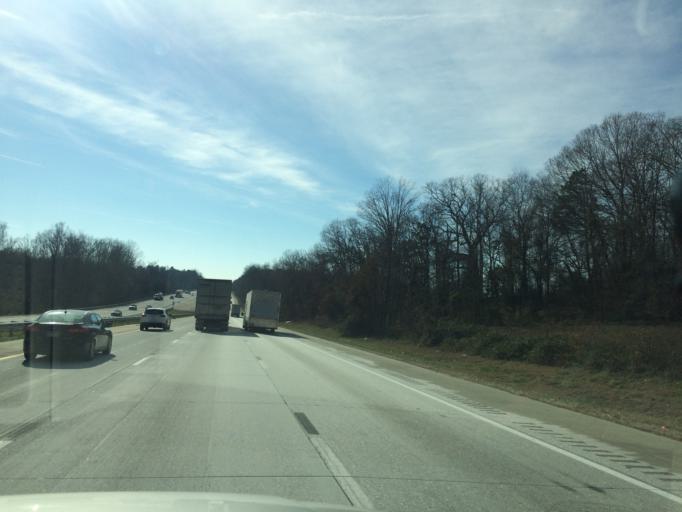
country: US
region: South Carolina
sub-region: Anderson County
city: Northlake
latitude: 34.6222
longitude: -82.6163
